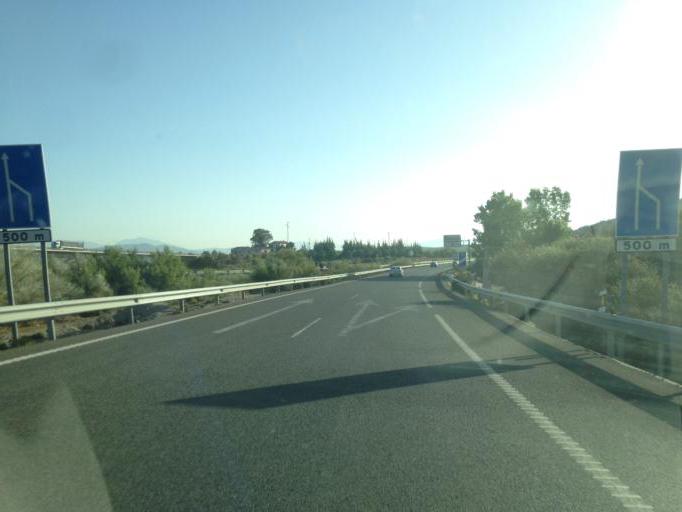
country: ES
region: Andalusia
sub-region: Provincia de Malaga
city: Villanueva de Tapia
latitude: 37.1267
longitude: -4.2910
